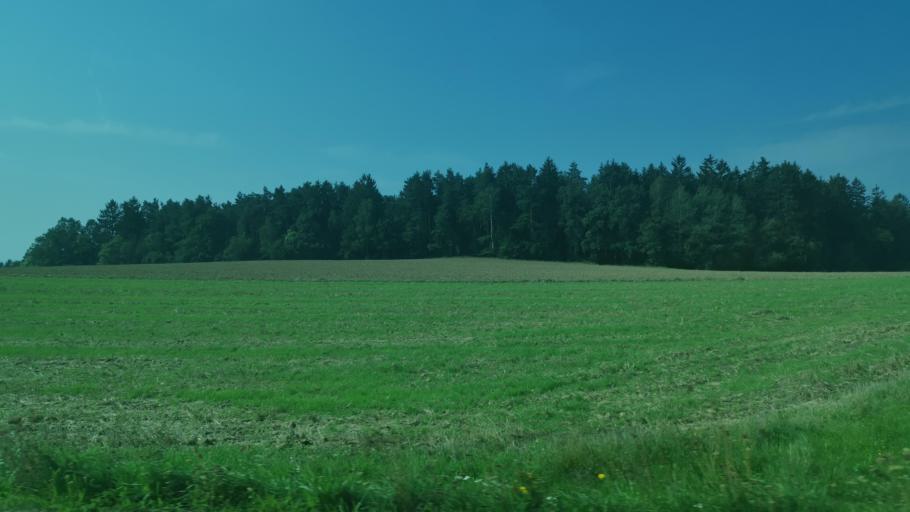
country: DE
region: Bavaria
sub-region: Upper Palatinate
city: Pemfling
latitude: 49.2630
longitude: 12.6327
